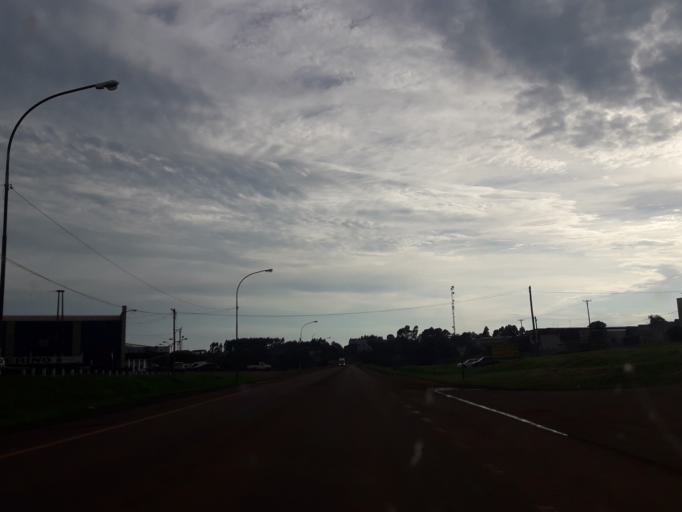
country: AR
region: Misiones
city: Dos de Mayo
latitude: -26.9904
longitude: -54.4845
